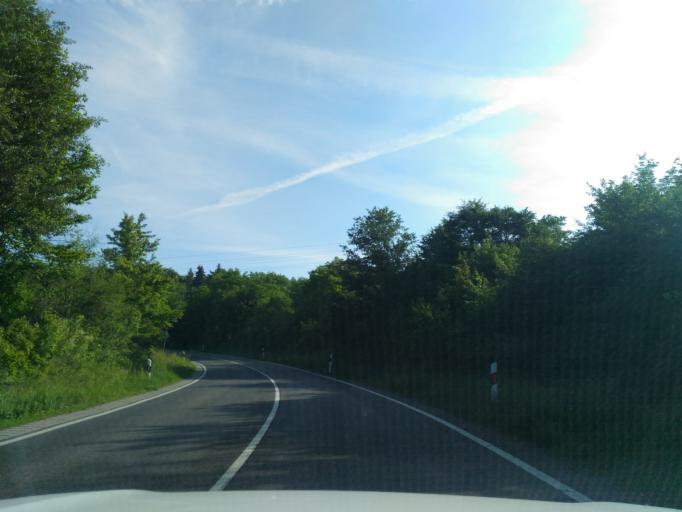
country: HU
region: Baranya
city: Komlo
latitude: 46.1718
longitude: 18.2626
